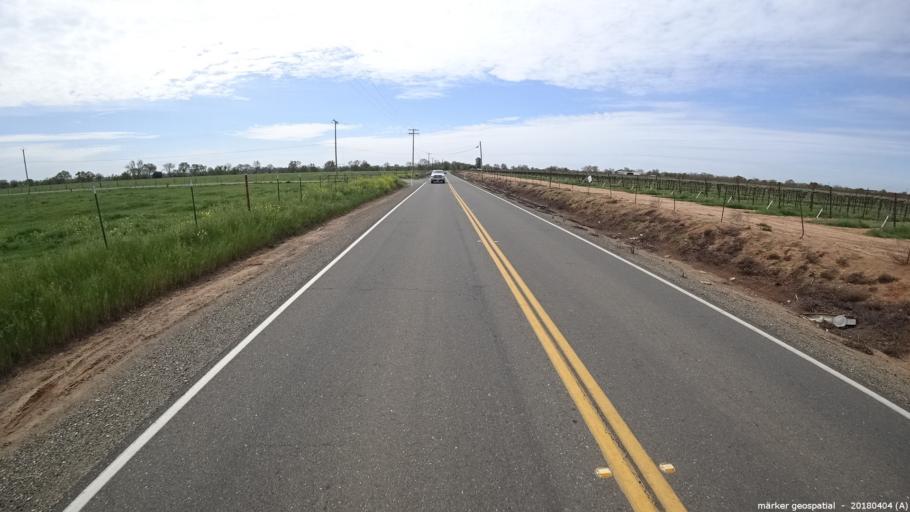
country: US
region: California
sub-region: Sacramento County
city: Clay
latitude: 38.2620
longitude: -121.1710
